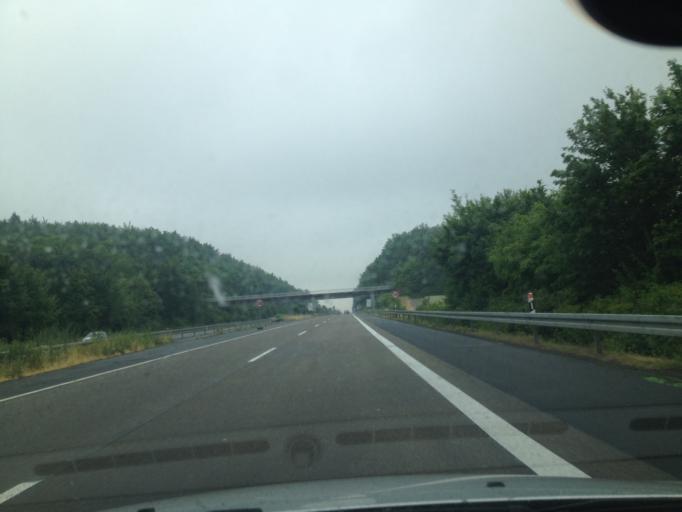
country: DE
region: Hesse
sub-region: Regierungsbezirk Darmstadt
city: Wolfersheim
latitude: 50.4284
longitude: 8.8026
